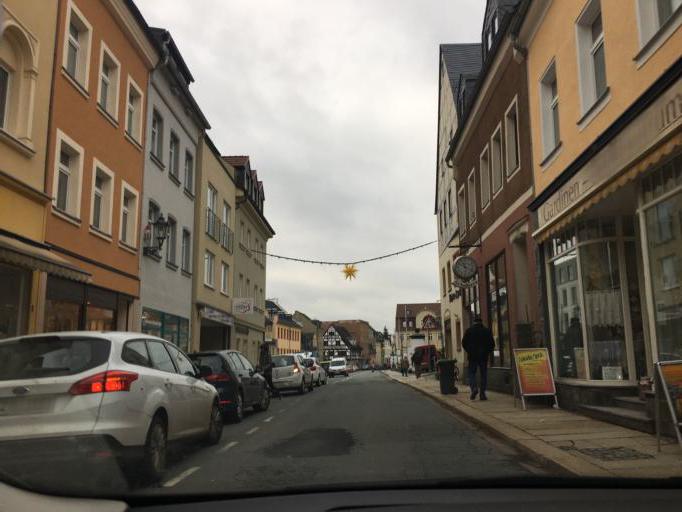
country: DE
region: Saxony
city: Hohenstein-Ernstthal
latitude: 50.8023
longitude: 12.7087
